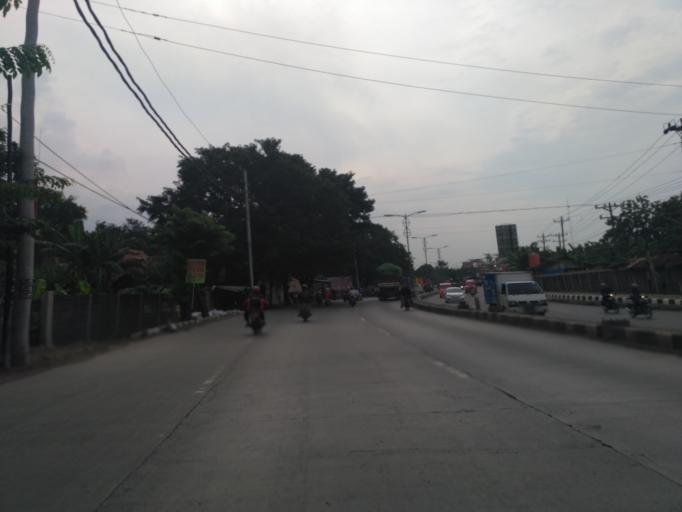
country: ID
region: Central Java
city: Semarang
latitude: -6.9744
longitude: 110.3149
